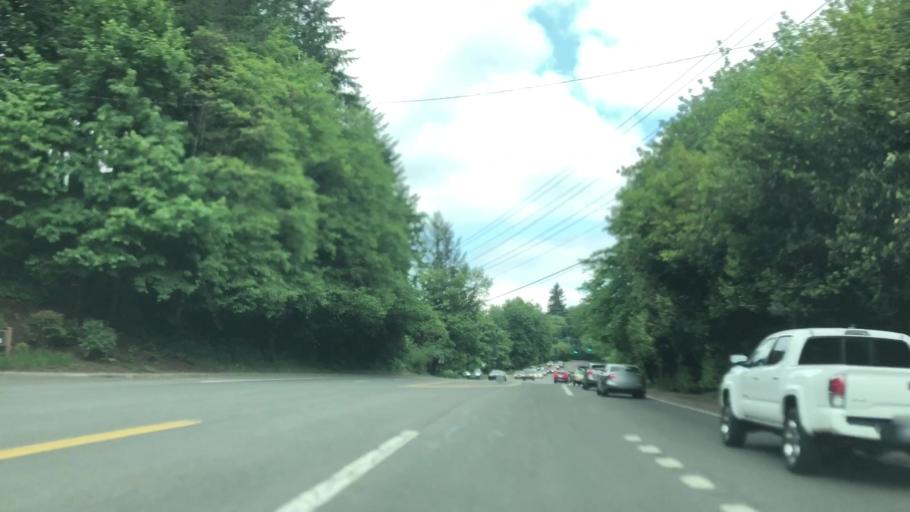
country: US
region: Oregon
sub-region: Clackamas County
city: Lake Oswego
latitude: 45.4231
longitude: -122.7091
